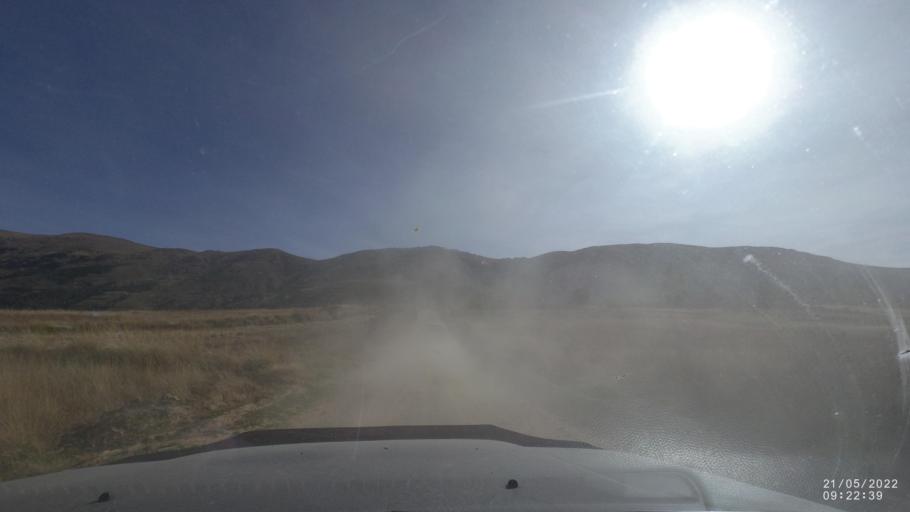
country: BO
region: Cochabamba
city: Colomi
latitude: -17.3480
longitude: -66.0143
